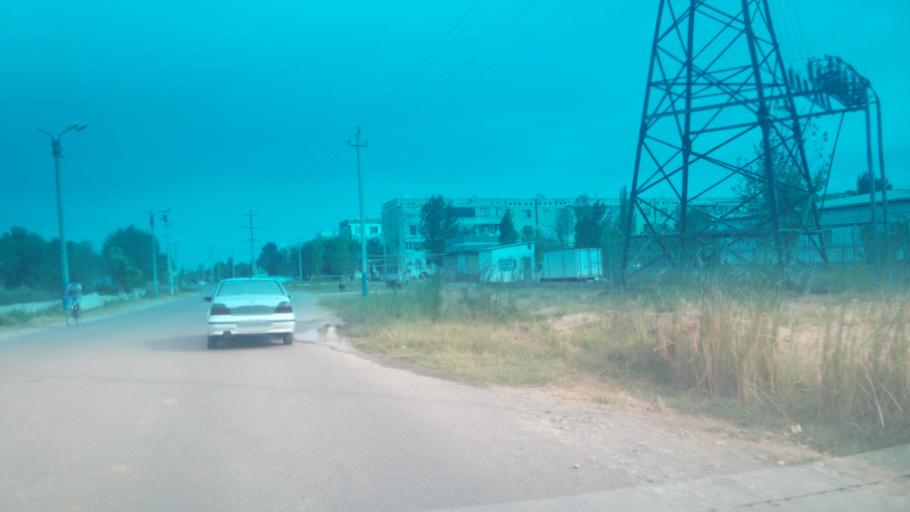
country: UZ
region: Sirdaryo
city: Guliston
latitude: 40.5132
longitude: 68.7768
